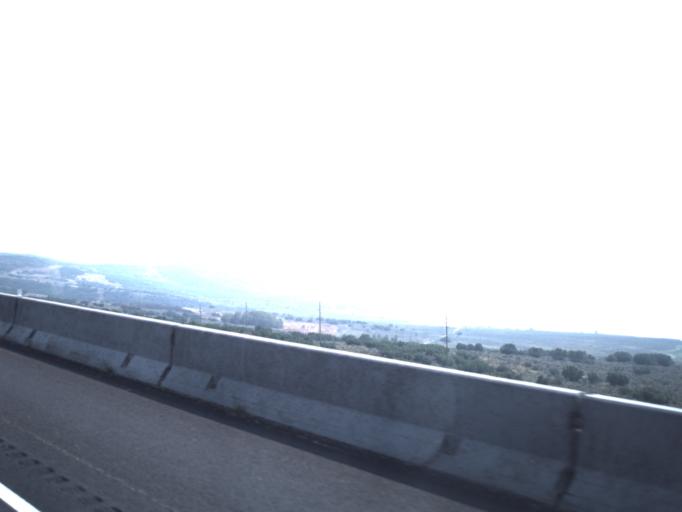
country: US
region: Utah
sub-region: Summit County
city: Park City
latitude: 40.6547
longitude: -111.4109
